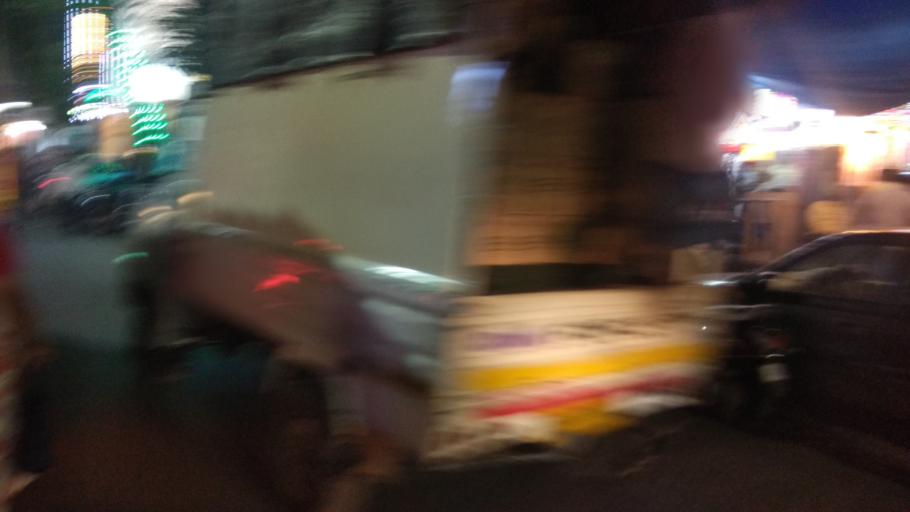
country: IN
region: Maharashtra
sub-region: Pune Division
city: Pune
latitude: 18.5174
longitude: 73.8594
